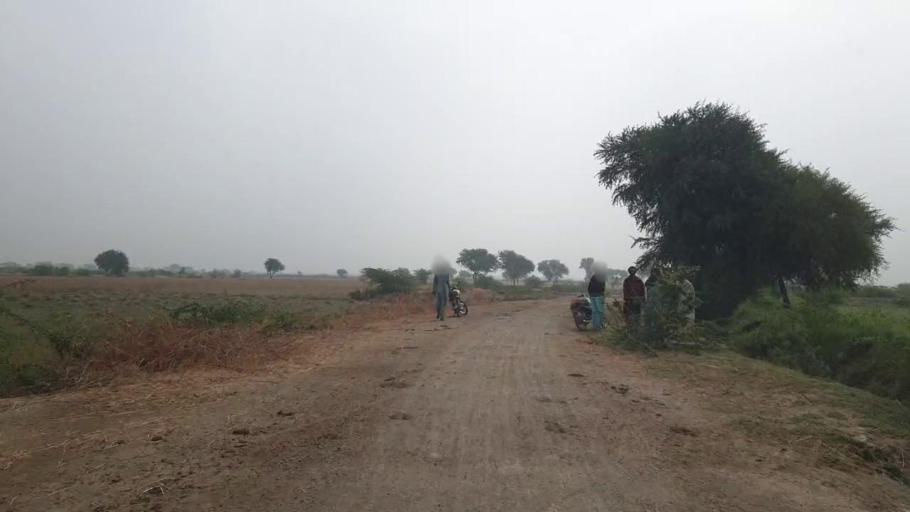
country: PK
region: Sindh
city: Badin
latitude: 24.5853
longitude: 68.6811
